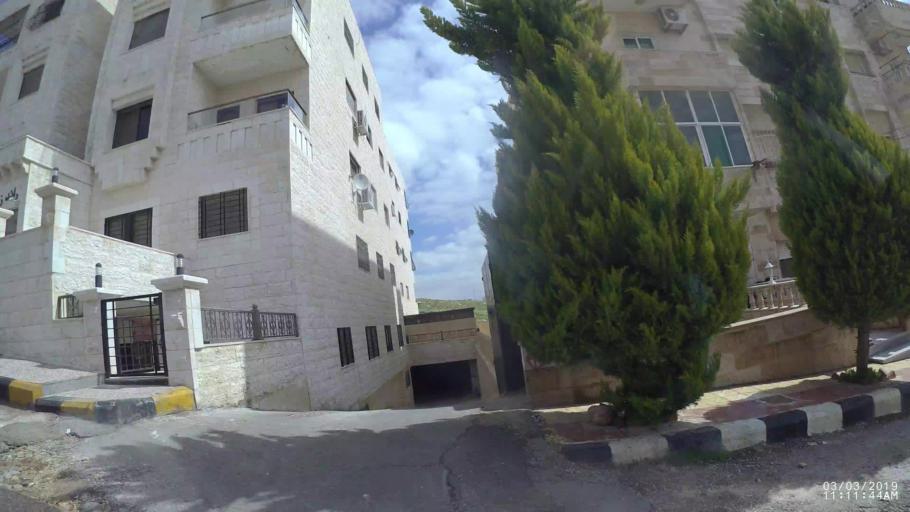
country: JO
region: Amman
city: Amman
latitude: 31.9972
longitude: 35.9160
